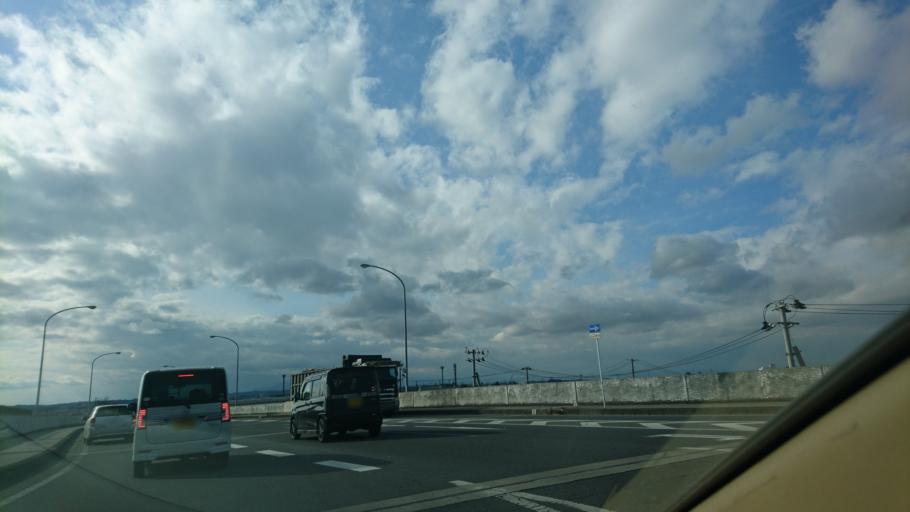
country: JP
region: Miyagi
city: Wakuya
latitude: 38.5317
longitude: 141.1409
